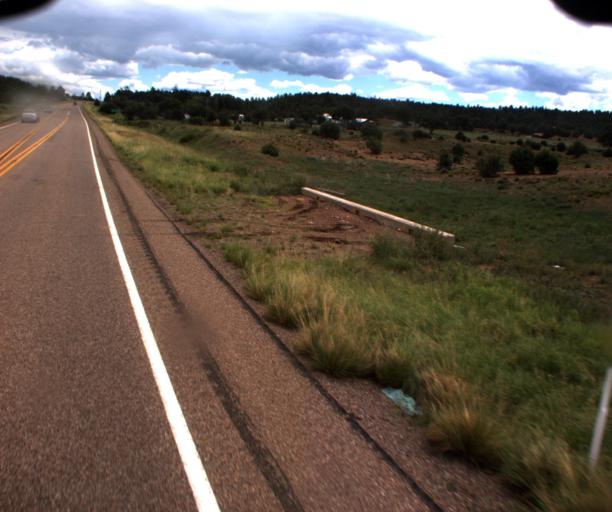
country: US
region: Arizona
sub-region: Navajo County
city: Linden
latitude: 34.3435
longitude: -110.2887
